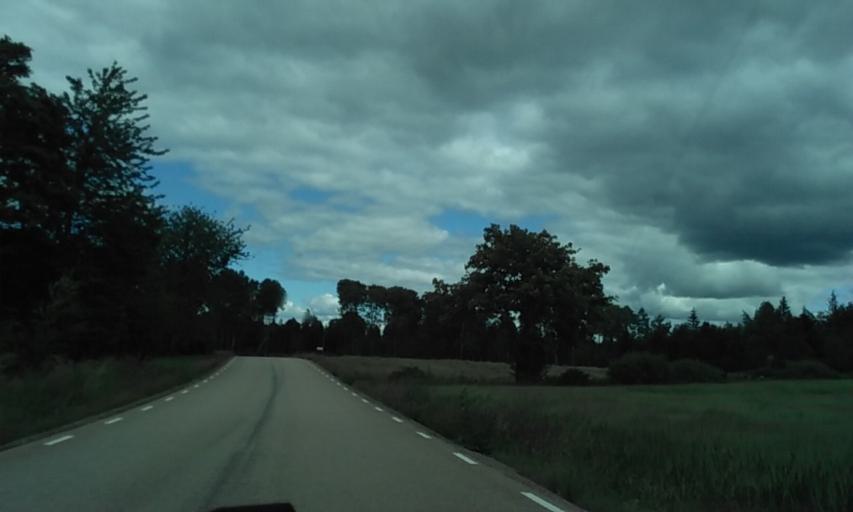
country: SE
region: Vaestra Goetaland
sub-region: Boras Kommun
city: Sjomarken
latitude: 57.7946
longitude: 12.8761
